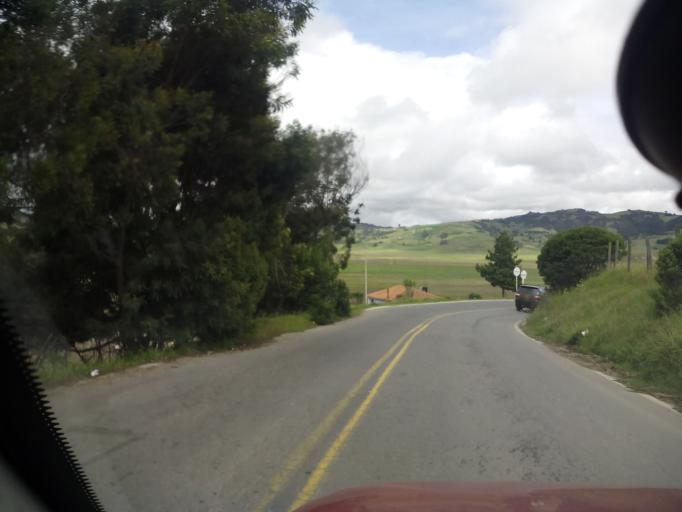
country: CO
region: Boyaca
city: Combita
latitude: 5.6360
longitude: -73.3489
